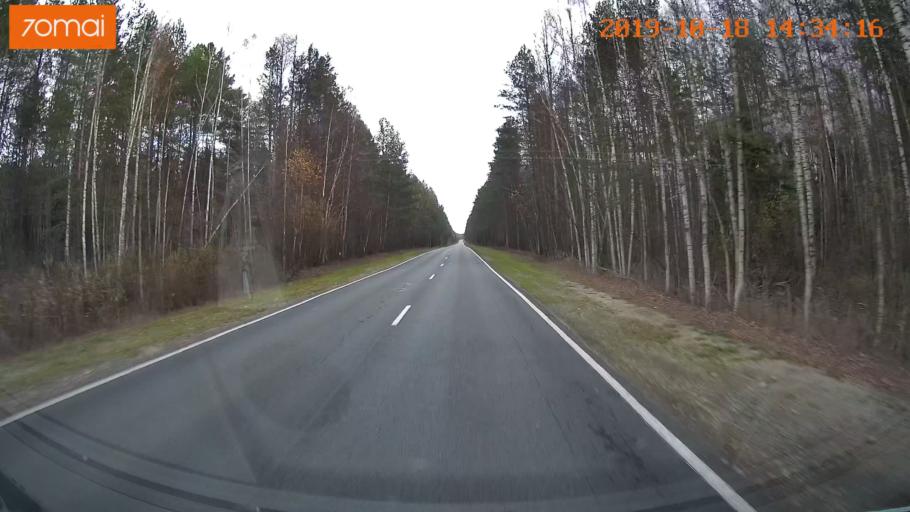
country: RU
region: Vladimir
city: Velikodvorskiy
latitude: 55.2104
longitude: 40.6130
